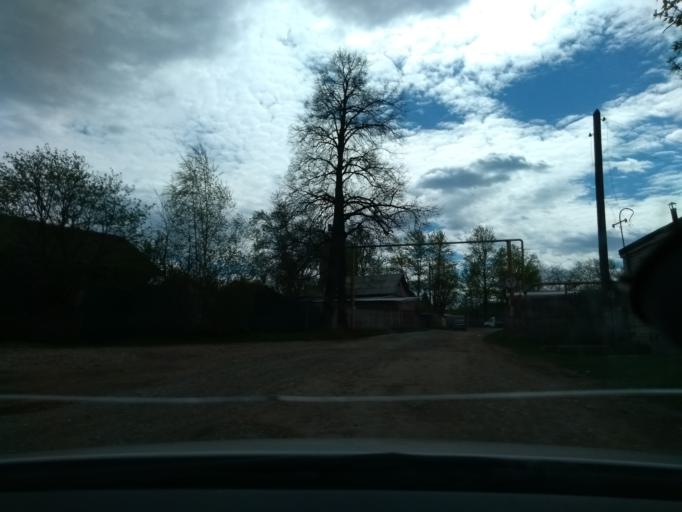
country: RU
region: Perm
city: Lobanovo
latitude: 57.8622
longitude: 56.3017
